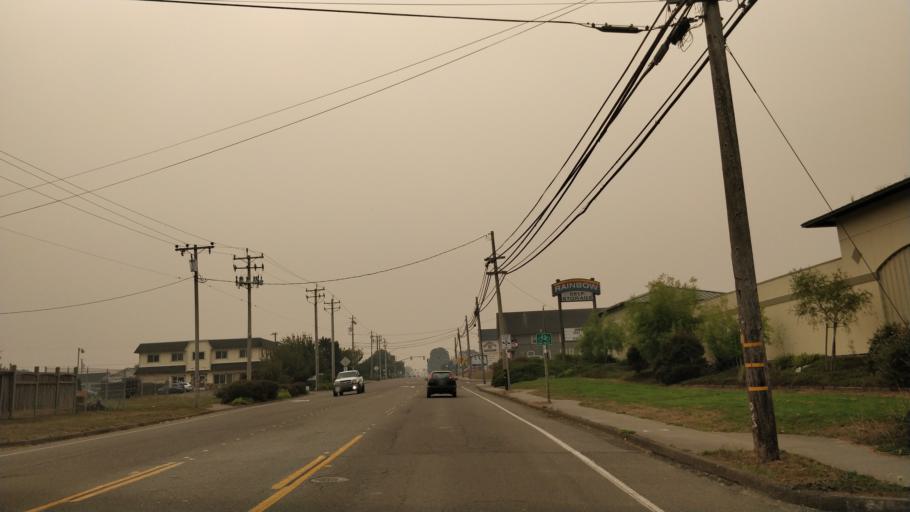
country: US
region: California
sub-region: Humboldt County
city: McKinleyville
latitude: 40.9491
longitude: -124.1010
